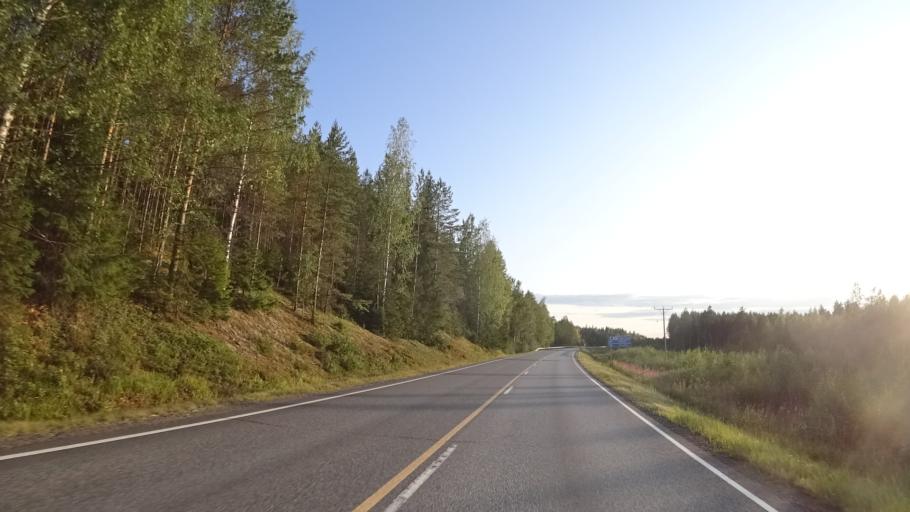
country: FI
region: South Karelia
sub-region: Lappeenranta
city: Ylaemaa
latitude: 60.8186
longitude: 28.0857
